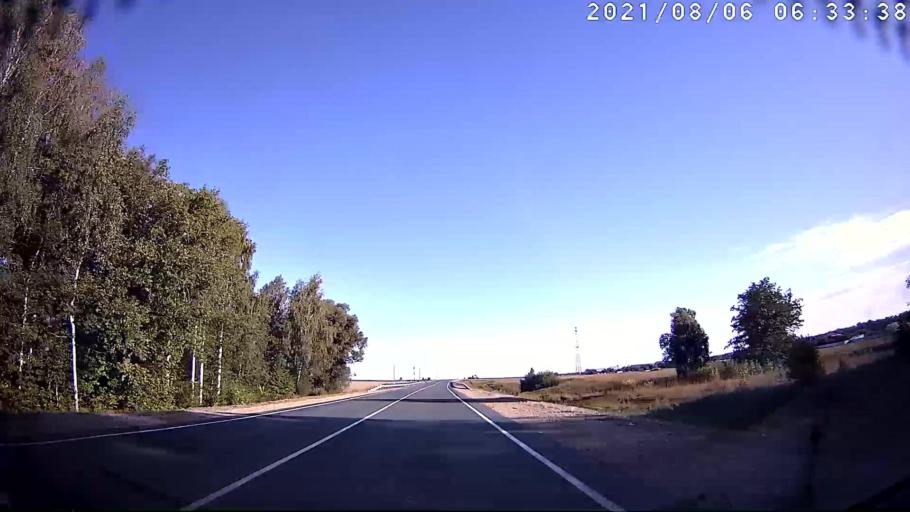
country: RU
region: Mariy-El
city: Krasnogorskiy
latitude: 56.1949
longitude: 48.2368
